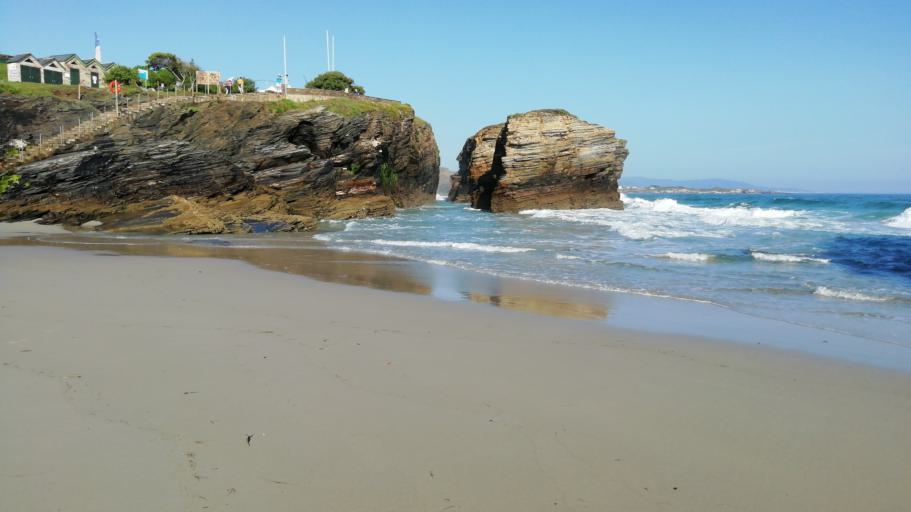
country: ES
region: Galicia
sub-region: Provincia de Lugo
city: Barreiros
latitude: 43.5540
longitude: -7.1576
